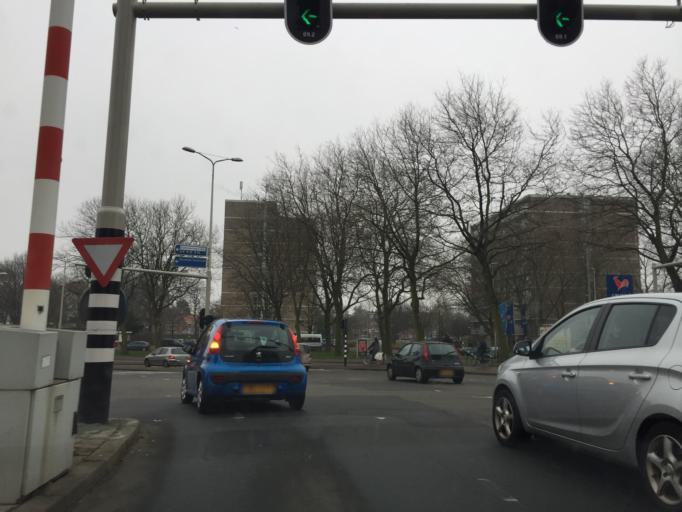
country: NL
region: South Holland
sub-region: Gemeente Den Haag
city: The Hague
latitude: 52.0614
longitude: 4.3160
